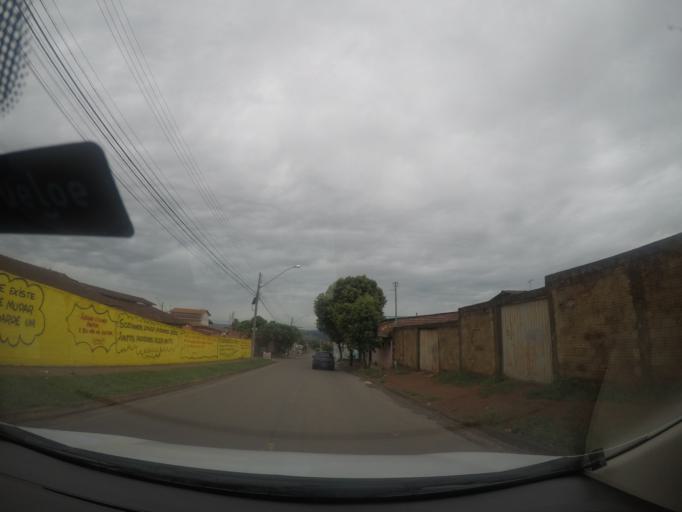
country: BR
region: Goias
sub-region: Goiania
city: Goiania
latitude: -16.6098
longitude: -49.3118
